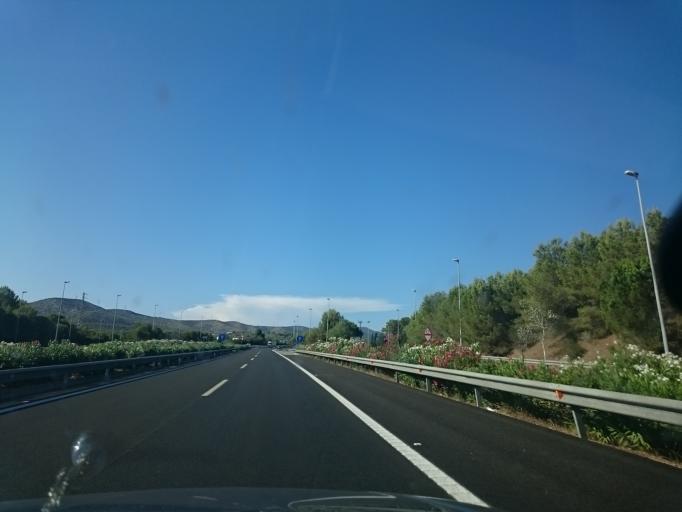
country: ES
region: Catalonia
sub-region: Provincia de Barcelona
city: Cubelles
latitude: 41.2261
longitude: 1.6775
